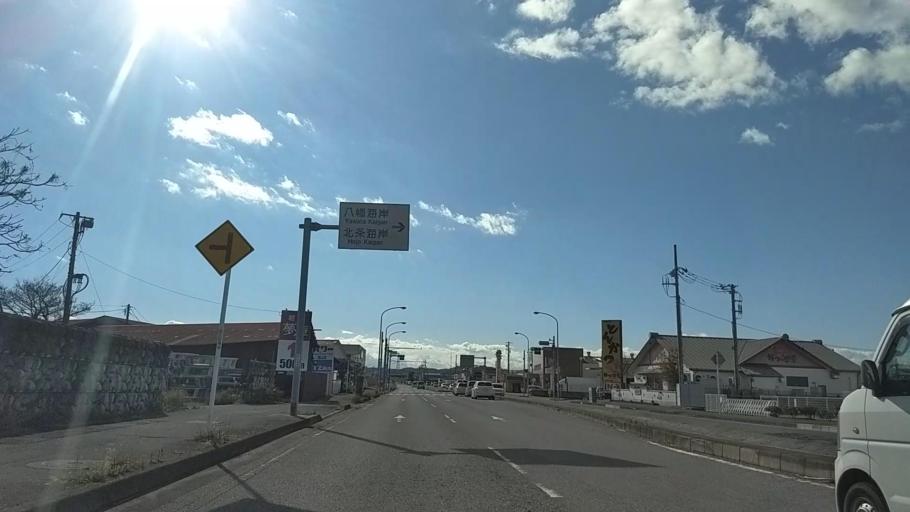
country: JP
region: Chiba
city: Tateyama
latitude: 35.0053
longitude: 139.8716
